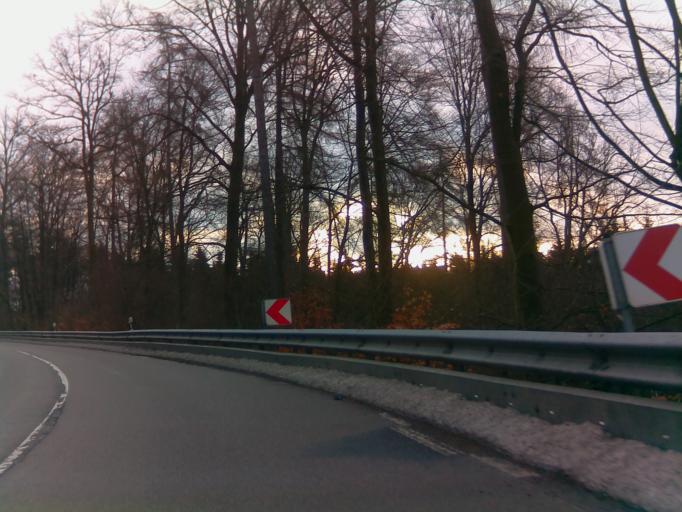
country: DE
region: Baden-Wuerttemberg
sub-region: Karlsruhe Region
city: Zwingenberg
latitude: 49.4461
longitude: 9.0384
